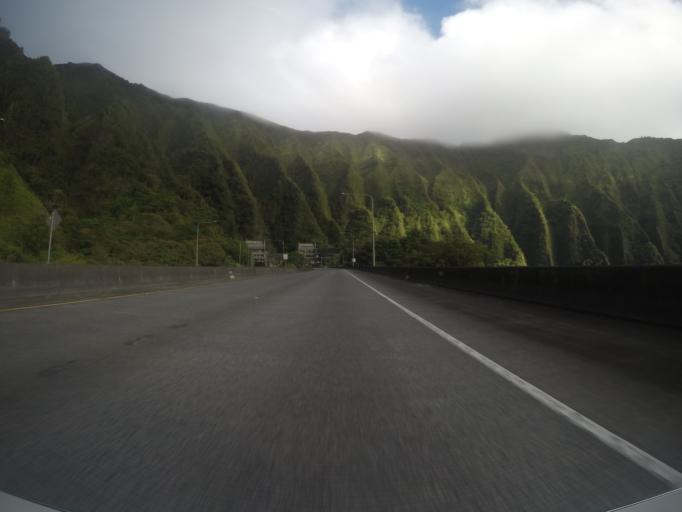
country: US
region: Hawaii
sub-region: Honolulu County
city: Kane'ohe
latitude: 21.4030
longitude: -157.8316
